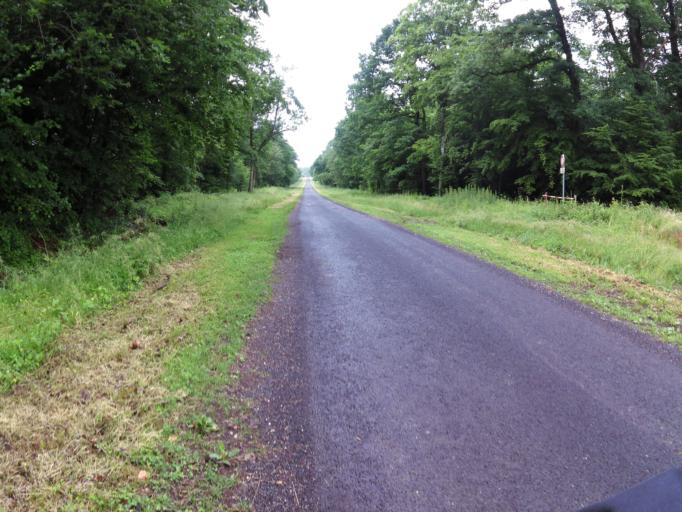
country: FR
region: Champagne-Ardenne
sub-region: Departement de la Marne
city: Sermaize-les-Bains
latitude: 48.7676
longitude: 4.9400
